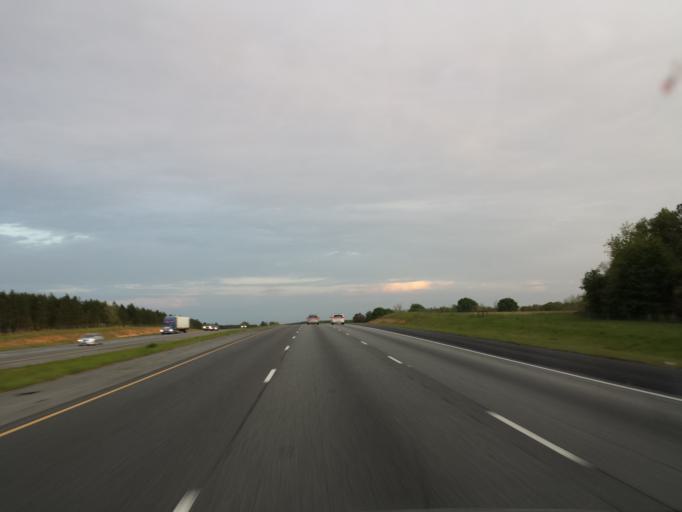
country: US
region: Georgia
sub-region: Turner County
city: Ashburn
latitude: 31.8189
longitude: -83.7097
